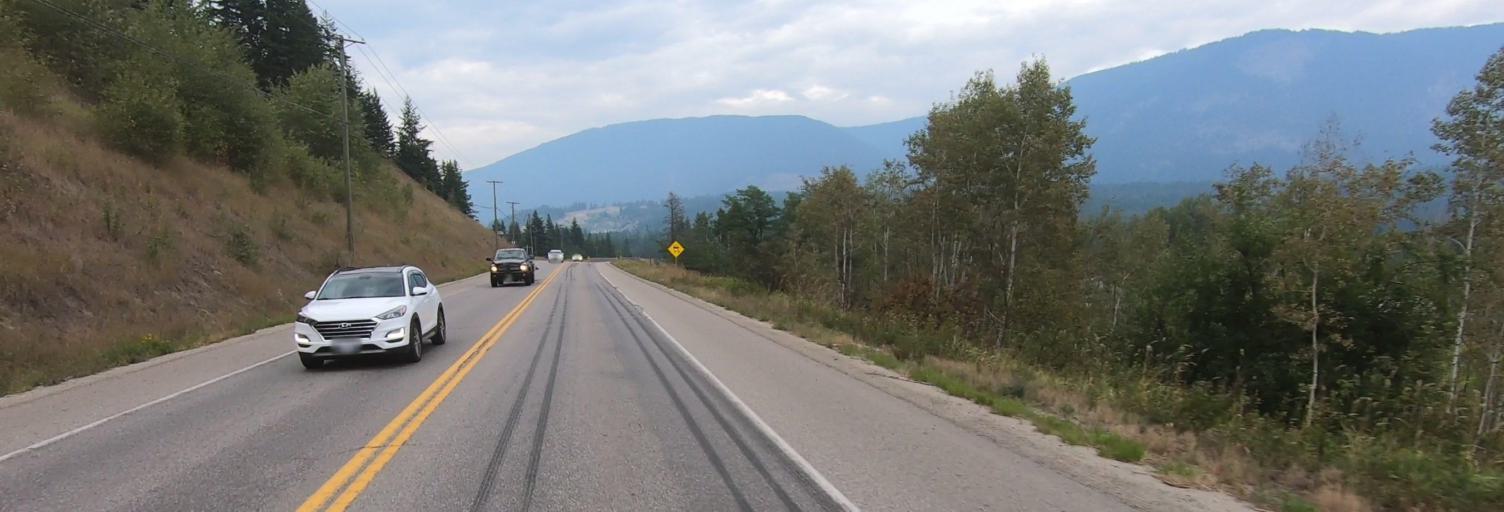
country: CA
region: British Columbia
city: Salmon Arm
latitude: 50.7829
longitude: -119.3361
